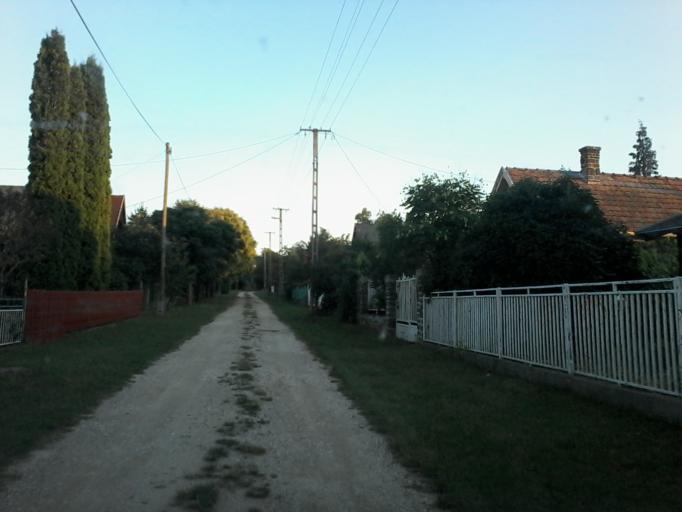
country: HU
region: Vas
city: Janoshaza
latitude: 47.1597
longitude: 17.0997
